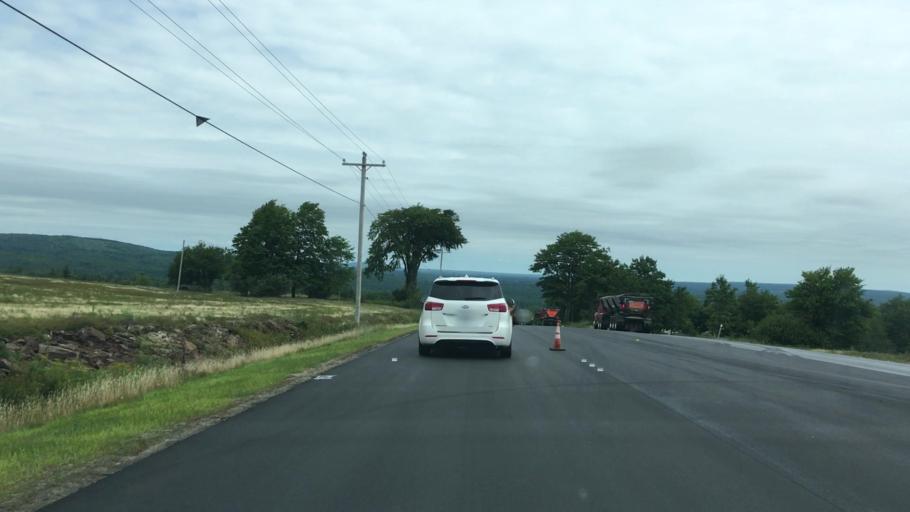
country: US
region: Maine
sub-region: Washington County
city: Machias
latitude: 44.9678
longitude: -67.6484
